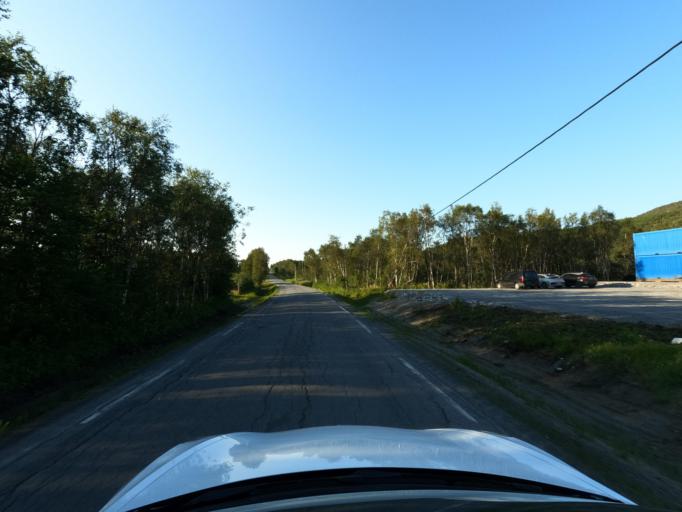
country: NO
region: Troms
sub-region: Skanland
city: Evenskjer
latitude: 68.4728
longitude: 16.7050
